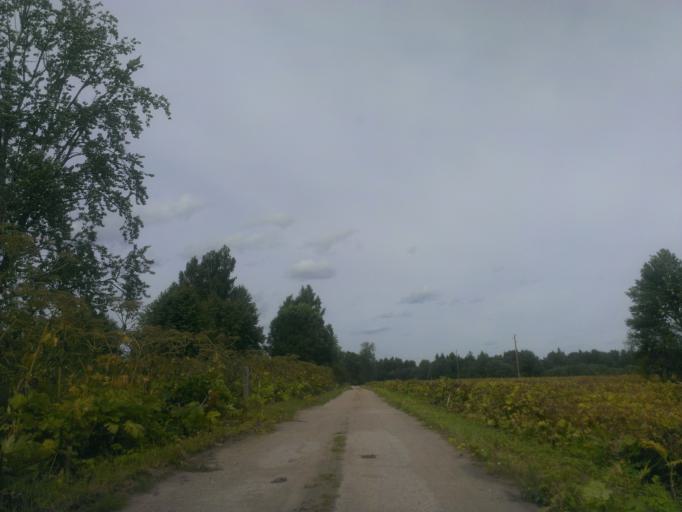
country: LV
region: Ligatne
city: Ligatne
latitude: 57.2270
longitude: 24.9567
